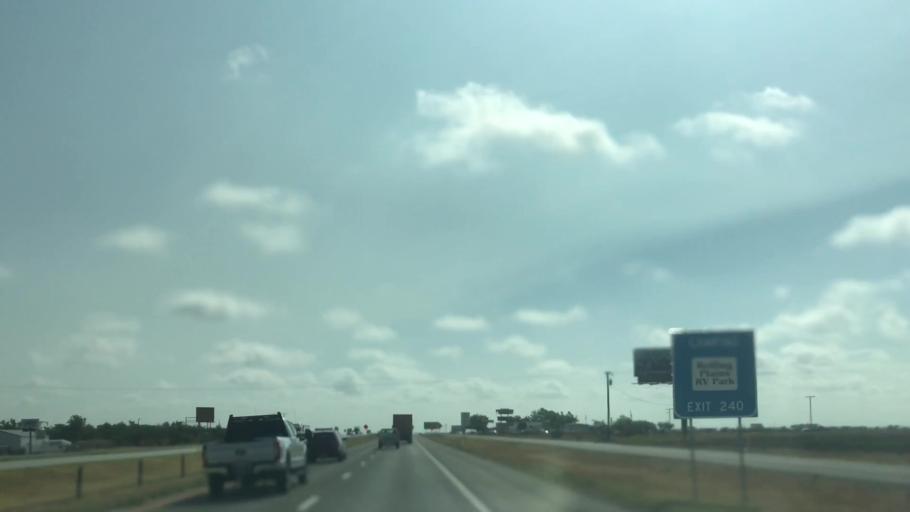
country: US
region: Texas
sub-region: Nolan County
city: Roscoe
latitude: 32.4495
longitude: -100.4873
